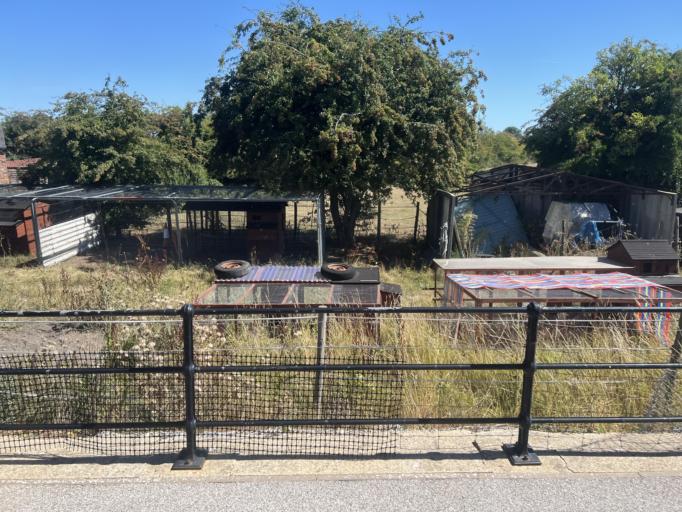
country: GB
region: England
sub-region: Lincolnshire
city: Wainfleet All Saints
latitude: 53.1229
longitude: 0.1998
